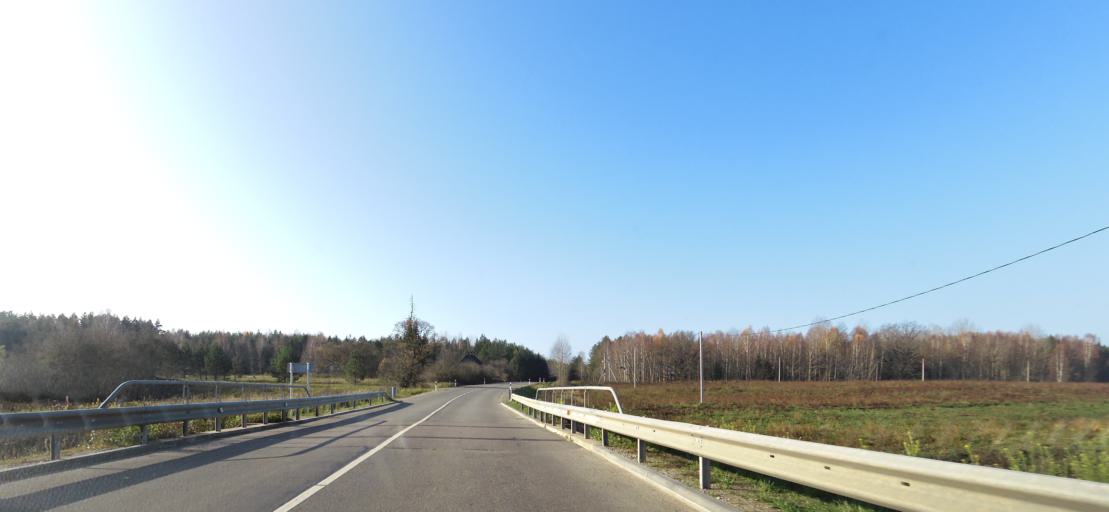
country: LT
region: Vilnius County
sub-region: Trakai
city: Rudiskes
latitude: 54.5093
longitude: 24.8756
